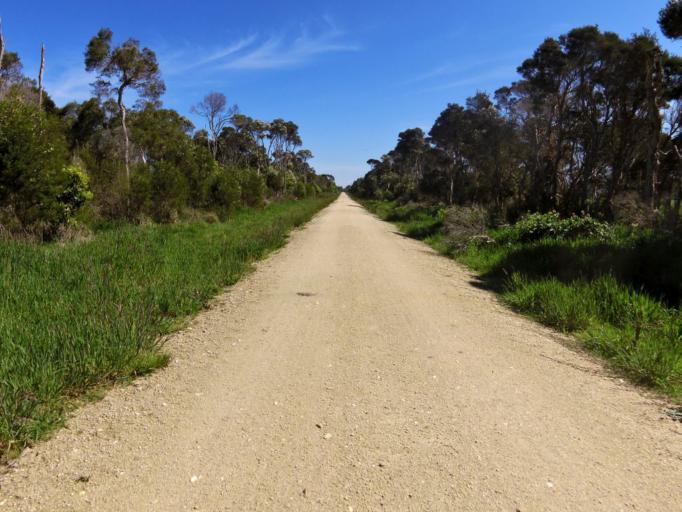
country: AU
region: Victoria
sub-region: Latrobe
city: Morwell
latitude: -38.6687
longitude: 146.4250
